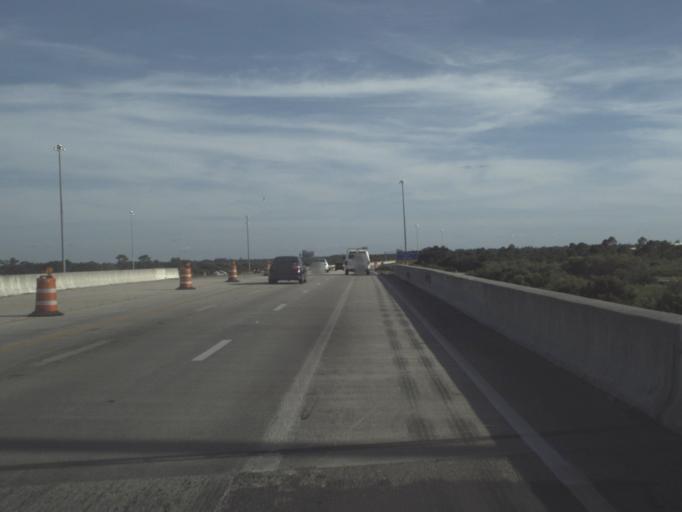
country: US
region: Florida
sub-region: Charlotte County
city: Harbour Heights
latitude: 26.9801
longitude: -82.0241
